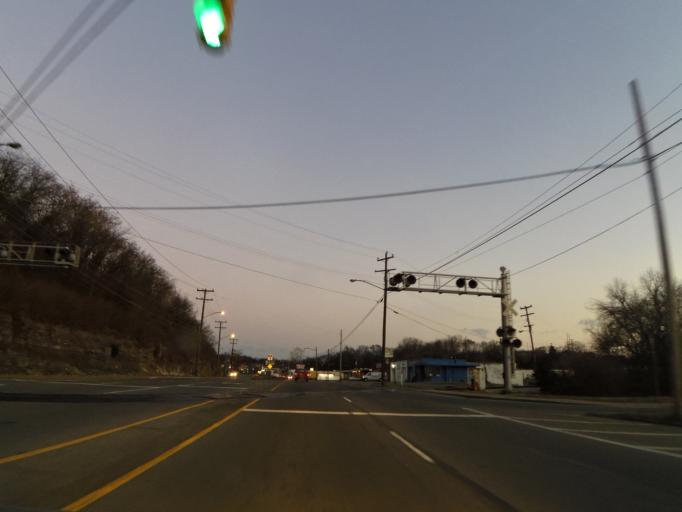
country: US
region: Tennessee
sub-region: Davidson County
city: Nashville
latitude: 36.1338
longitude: -86.7589
